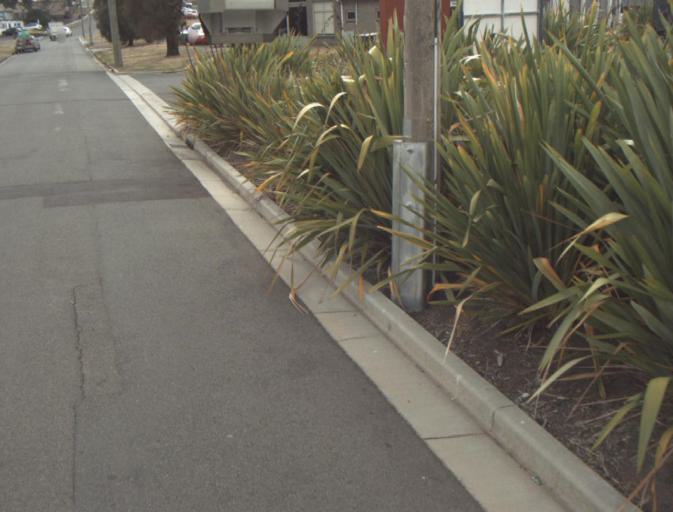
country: AU
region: Tasmania
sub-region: Launceston
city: Summerhill
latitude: -41.4763
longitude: 147.1619
